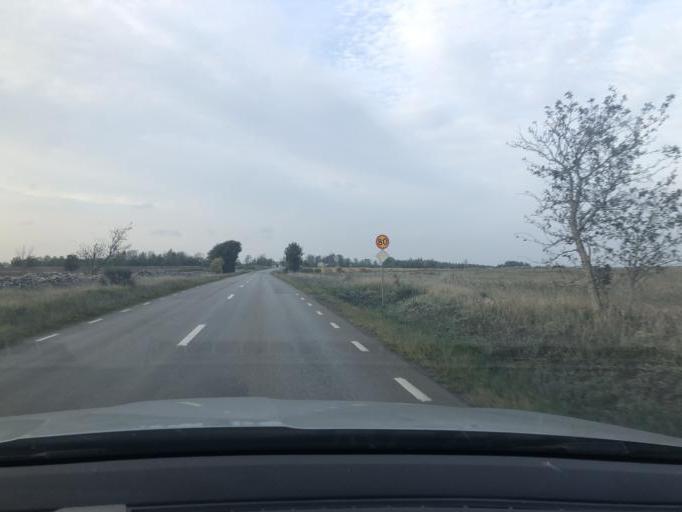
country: SE
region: Kalmar
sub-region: Morbylanga Kommun
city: Moerbylanga
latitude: 56.4081
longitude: 16.4360
